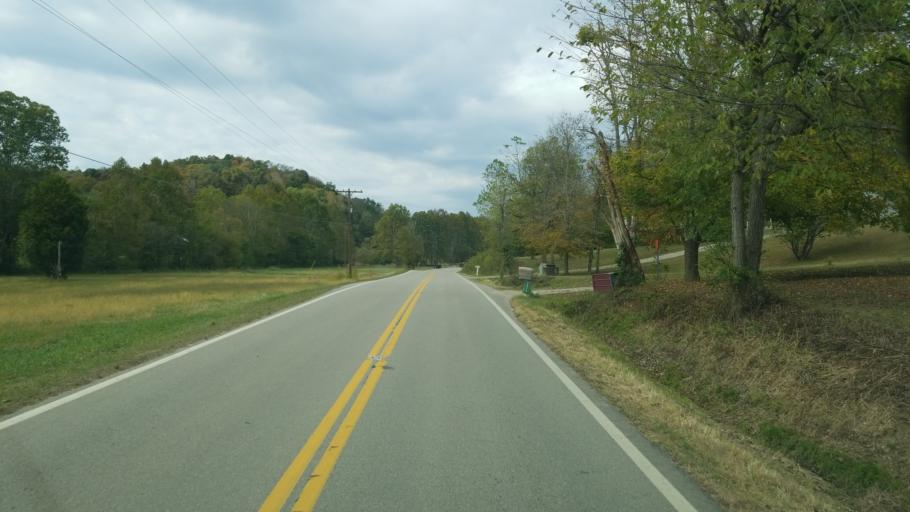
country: US
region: Ohio
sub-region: Meigs County
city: Pomeroy
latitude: 39.0762
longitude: -82.0847
